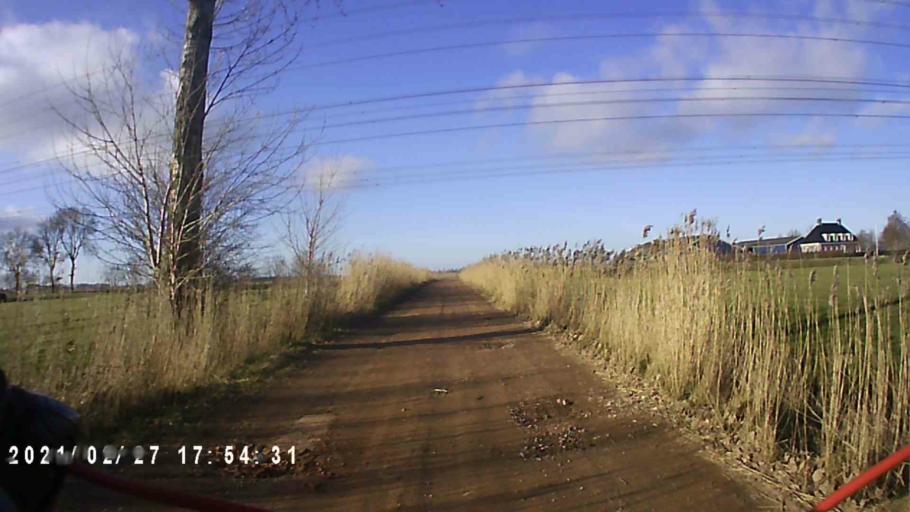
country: NL
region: Groningen
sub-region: Gemeente Bedum
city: Bedum
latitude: 53.3134
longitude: 6.6158
